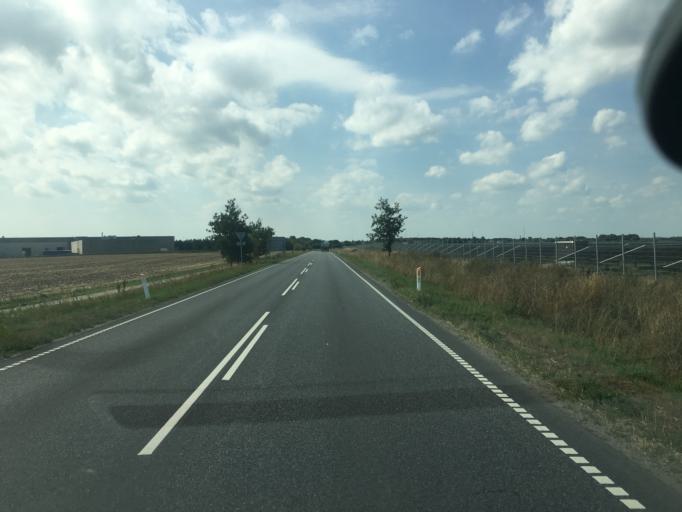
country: DK
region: South Denmark
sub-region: Aabenraa Kommune
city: Tinglev
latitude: 54.9487
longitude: 9.2750
